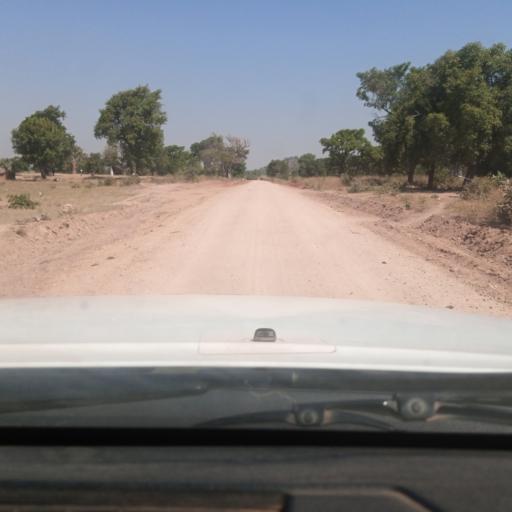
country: NG
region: Adamawa
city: Yola
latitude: 9.0613
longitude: 12.3867
